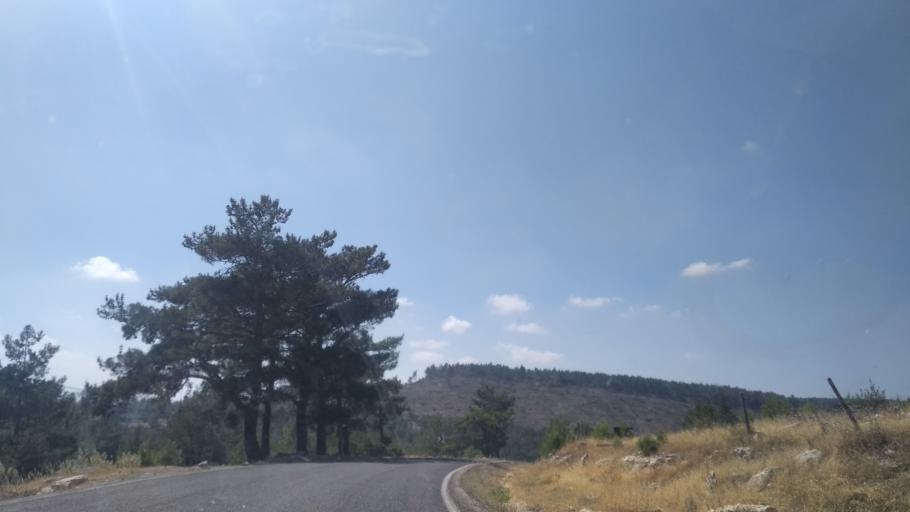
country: TR
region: Mersin
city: Gulnar
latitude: 36.3034
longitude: 33.4569
